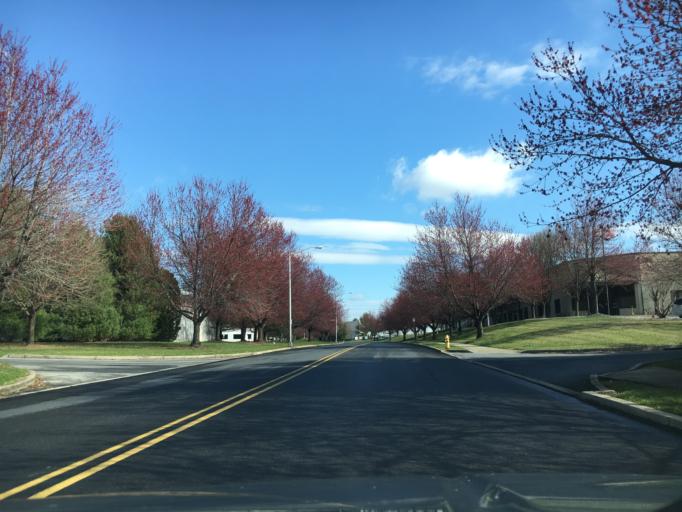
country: US
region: Pennsylvania
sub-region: Northampton County
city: Bath
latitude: 40.6758
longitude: -75.3832
